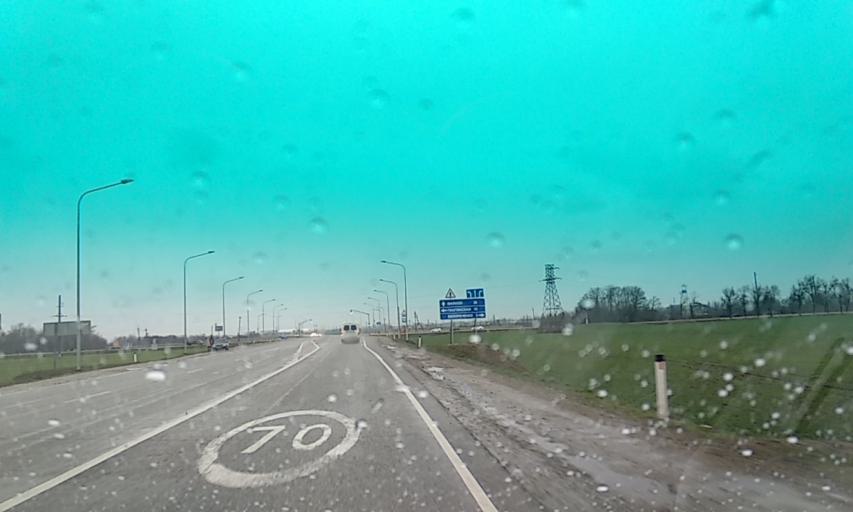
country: RU
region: Krasnodarskiy
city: Belorechensk
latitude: 44.8151
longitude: 39.8538
